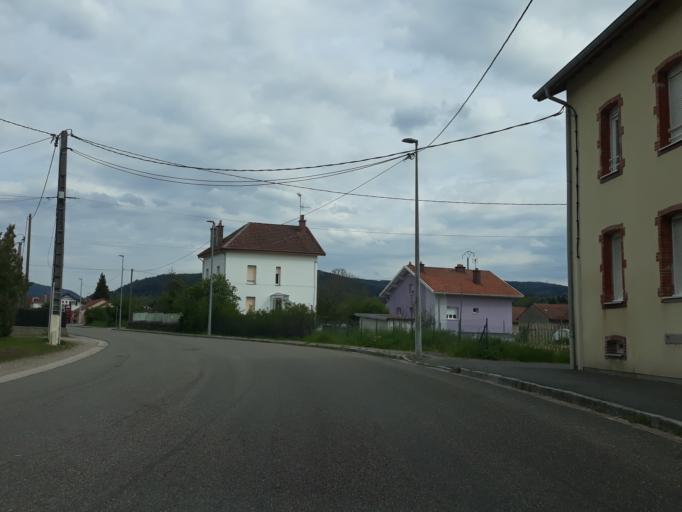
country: FR
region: Lorraine
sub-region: Departement des Vosges
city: Granges-sur-Vologne
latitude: 48.1474
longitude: 6.7831
